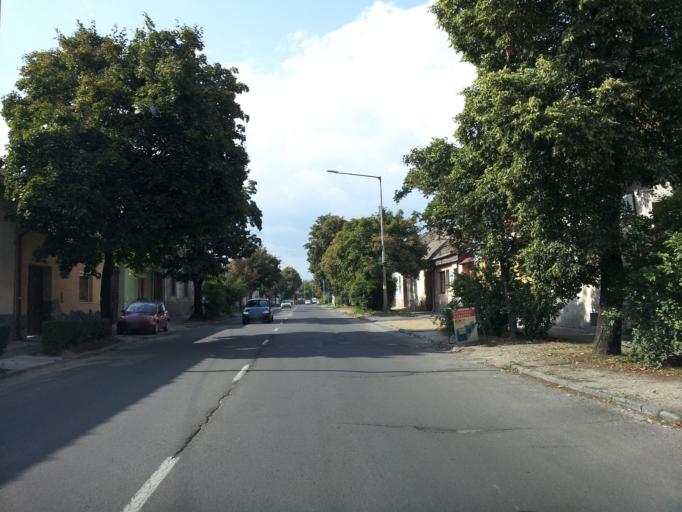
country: HU
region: Pest
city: Vac
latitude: 47.7858
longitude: 19.1219
